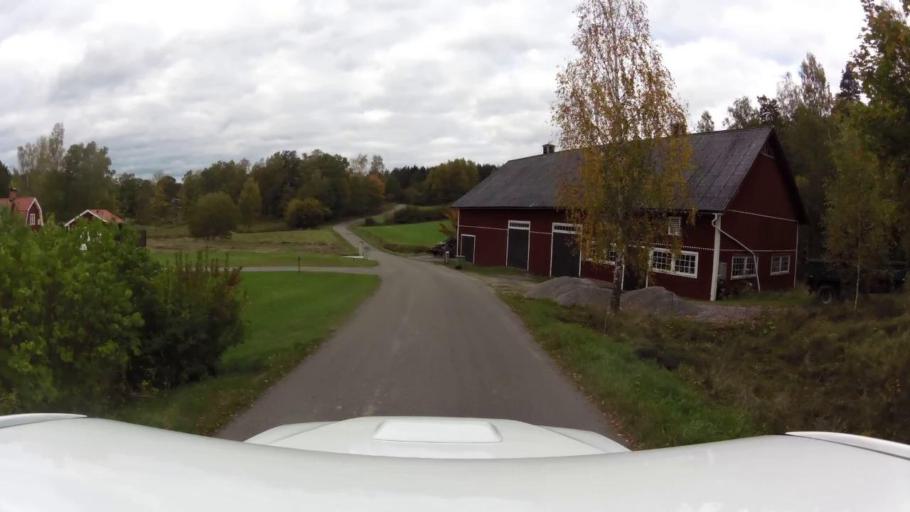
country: SE
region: OEstergoetland
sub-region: Kinda Kommun
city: Rimforsa
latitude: 58.1955
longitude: 15.5941
